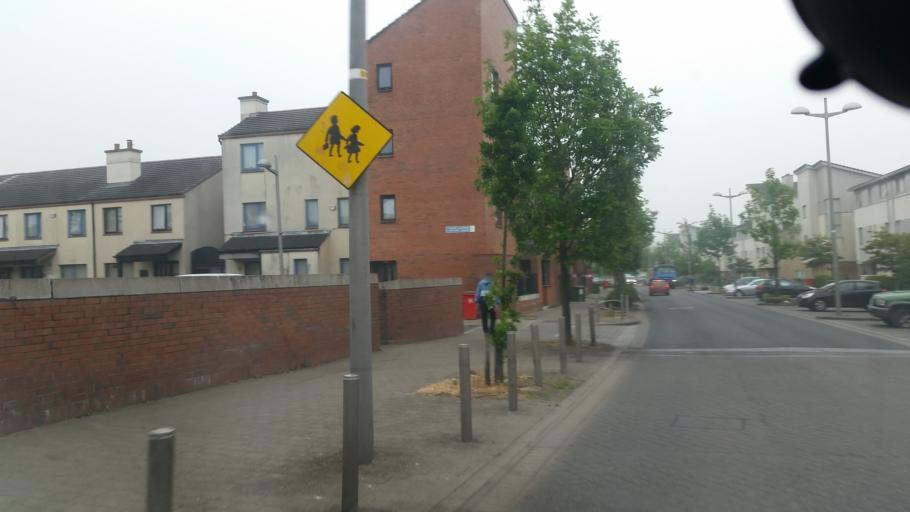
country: IE
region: Leinster
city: Ballymun
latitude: 53.3988
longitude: -6.2749
